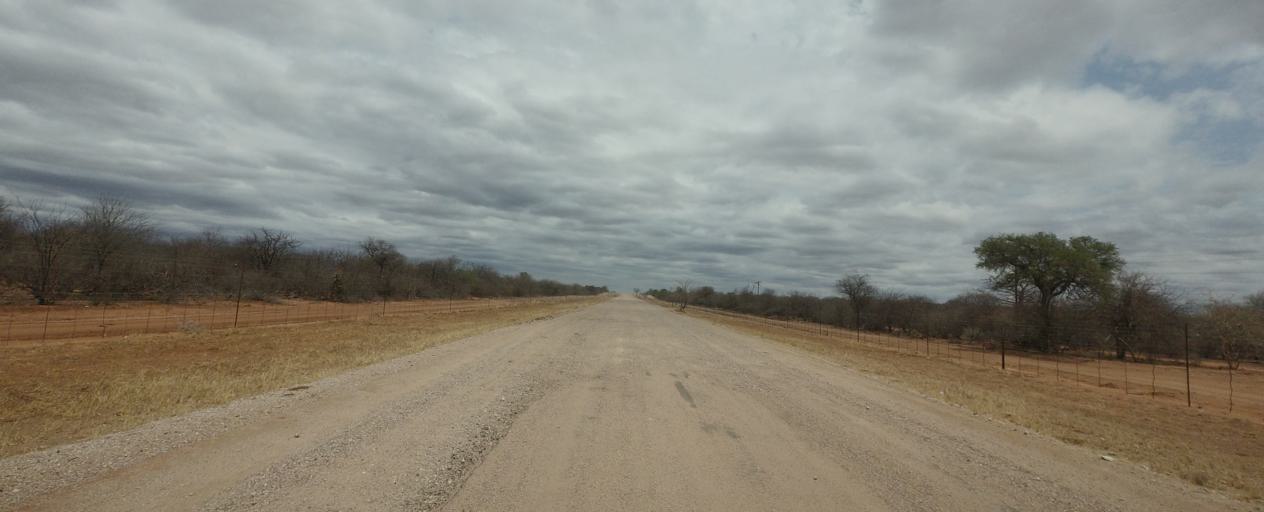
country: BW
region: Central
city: Mathathane
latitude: -22.6893
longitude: 28.6410
